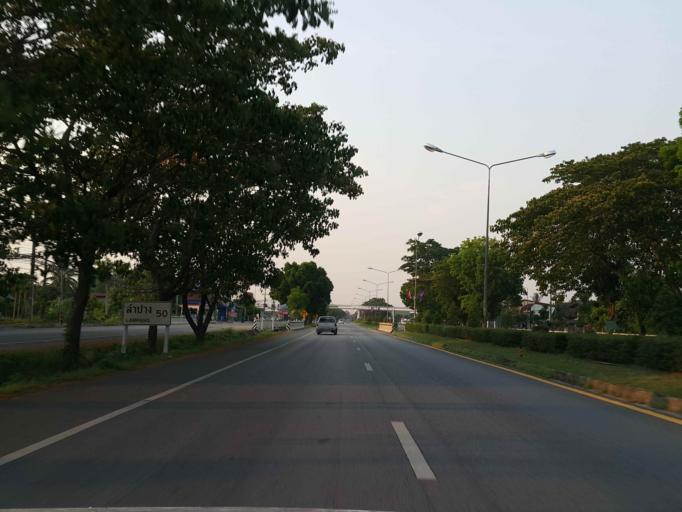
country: TH
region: Lampang
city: Sop Prap
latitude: 17.8879
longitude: 99.3391
